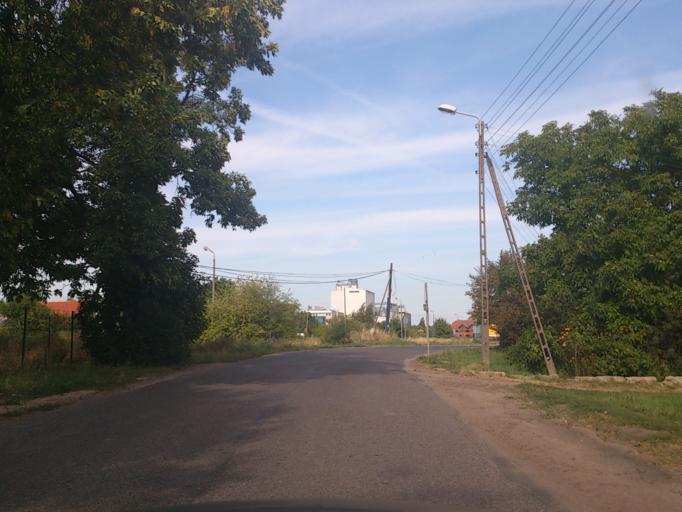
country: PL
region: Kujawsko-Pomorskie
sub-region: Powiat golubsko-dobrzynski
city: Golub-Dobrzyn
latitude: 53.1192
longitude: 19.0431
